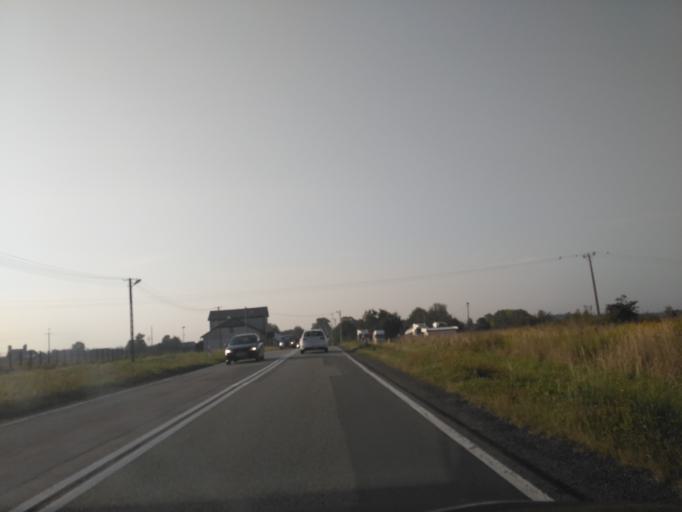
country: PL
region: Lublin Voivodeship
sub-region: Powiat krasnicki
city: Szastarka
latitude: 50.8296
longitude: 22.3082
